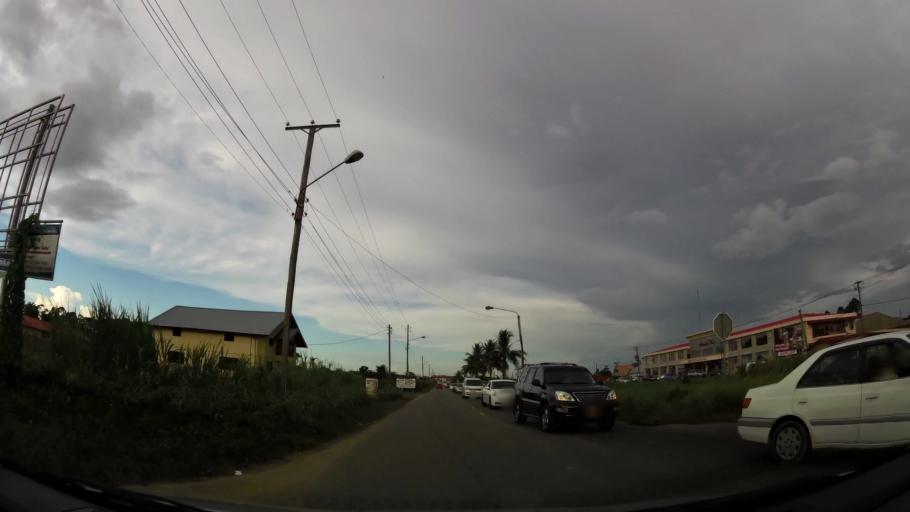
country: SR
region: Paramaribo
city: Paramaribo
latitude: 5.8566
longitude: -55.1664
